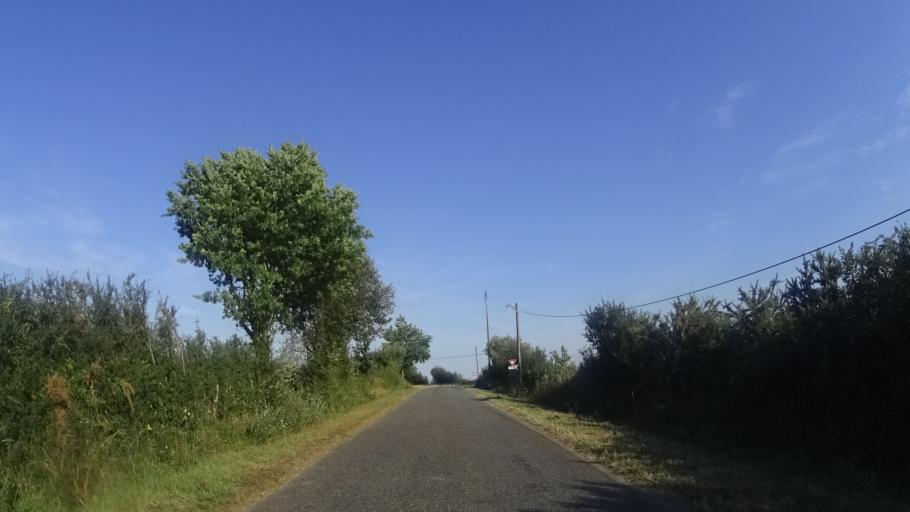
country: FR
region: Pays de la Loire
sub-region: Departement de la Loire-Atlantique
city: Mouzeil
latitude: 47.4886
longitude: -1.3686
